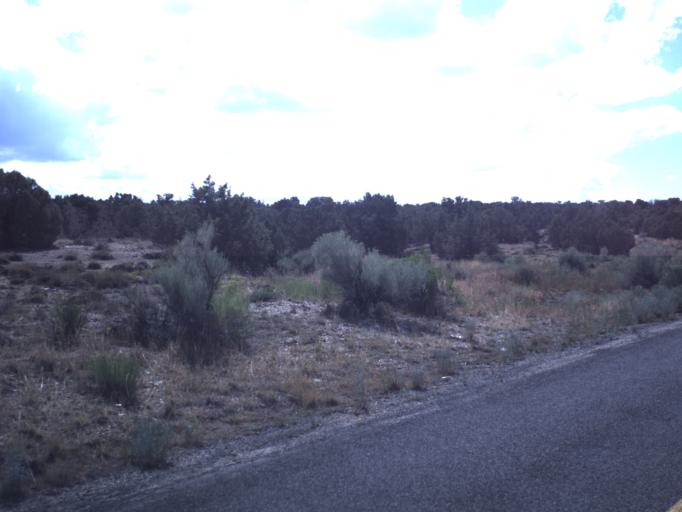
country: US
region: Utah
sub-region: Duchesne County
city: Duchesne
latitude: 40.1774
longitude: -110.4494
